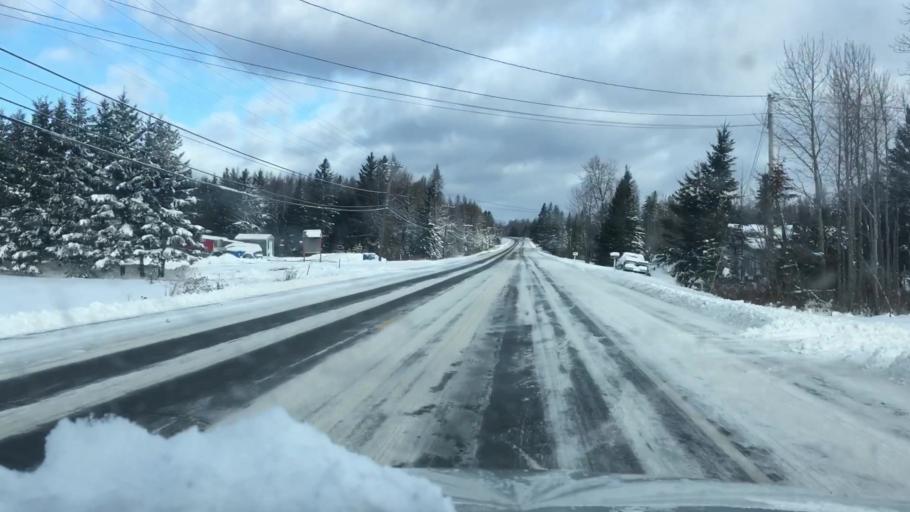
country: US
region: Maine
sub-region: Aroostook County
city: Caribou
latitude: 46.9184
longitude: -68.0190
